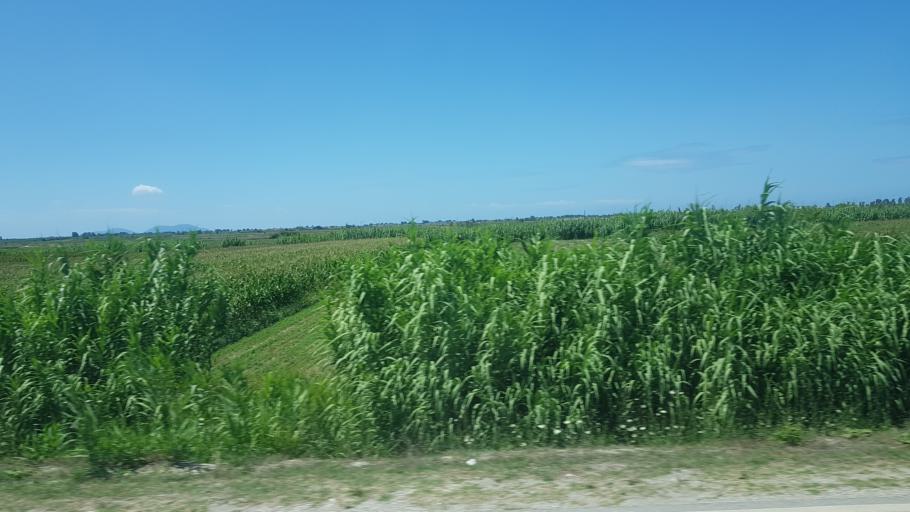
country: AL
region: Fier
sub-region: Rrethi i Fierit
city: Frakulla e Madhe
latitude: 40.6565
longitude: 19.4910
